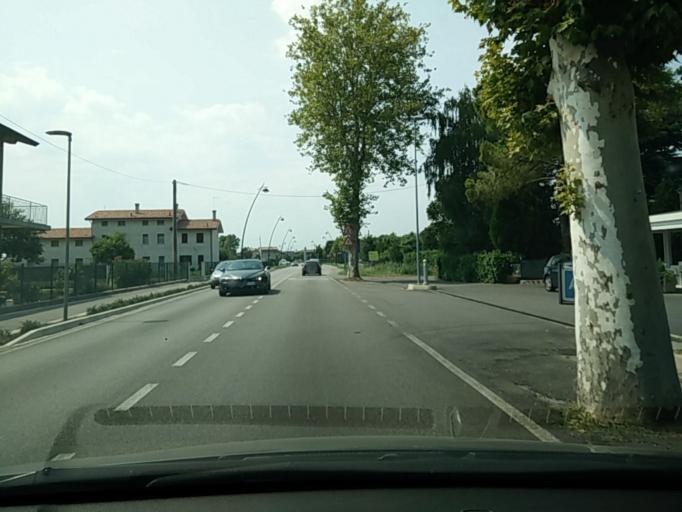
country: IT
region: Veneto
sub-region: Provincia di Venezia
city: Eraclea
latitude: 45.5838
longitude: 12.6822
